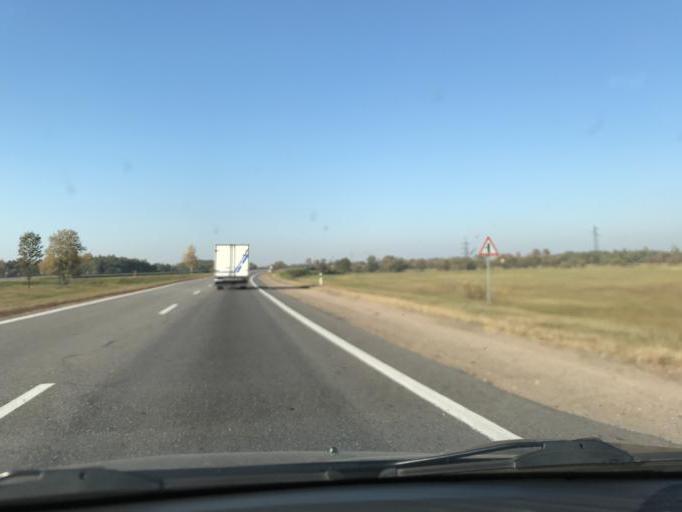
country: BY
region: Minsk
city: Dukora
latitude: 53.6607
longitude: 27.9467
